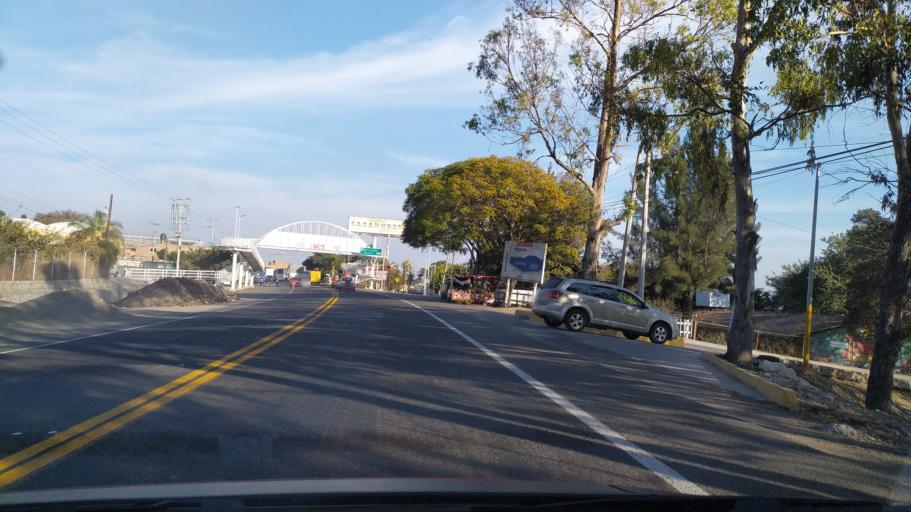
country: MX
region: Jalisco
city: Jamay
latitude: 20.2919
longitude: -102.7222
